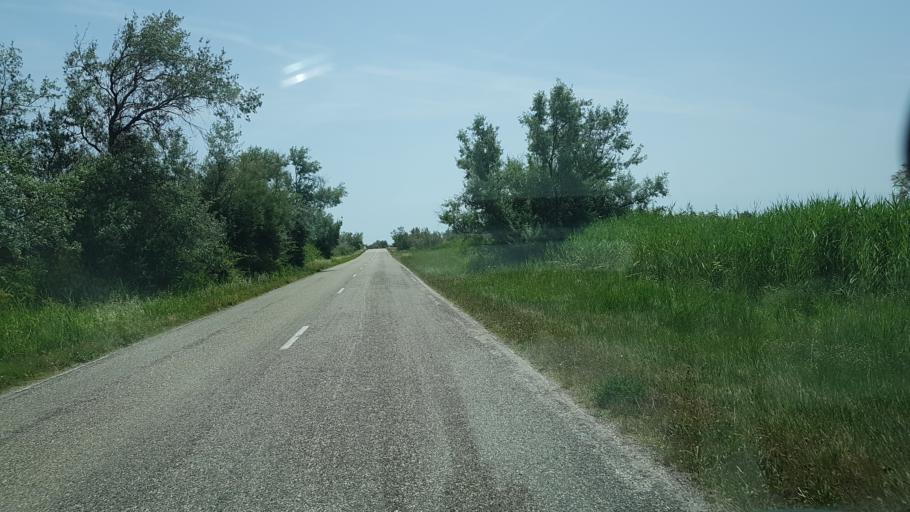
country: FR
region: Languedoc-Roussillon
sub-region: Departement du Gard
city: Saint-Gilles
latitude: 43.5749
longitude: 4.5242
